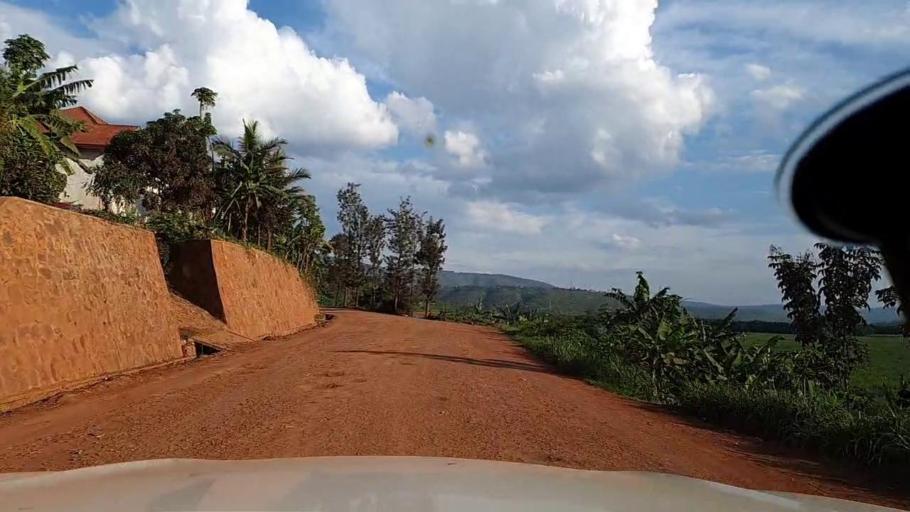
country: RW
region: Kigali
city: Kigali
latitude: -1.9296
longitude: 29.9930
